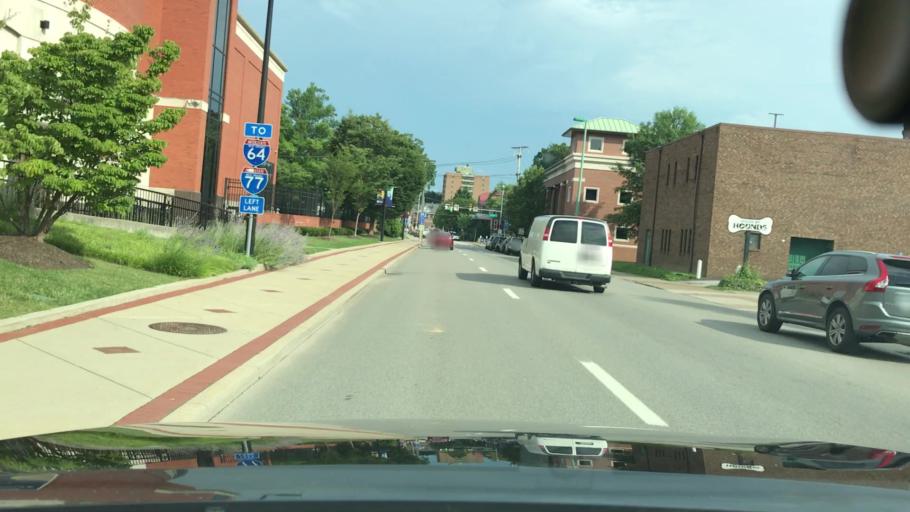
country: US
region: West Virginia
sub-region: Kanawha County
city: Charleston
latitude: 38.3480
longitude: -81.6302
